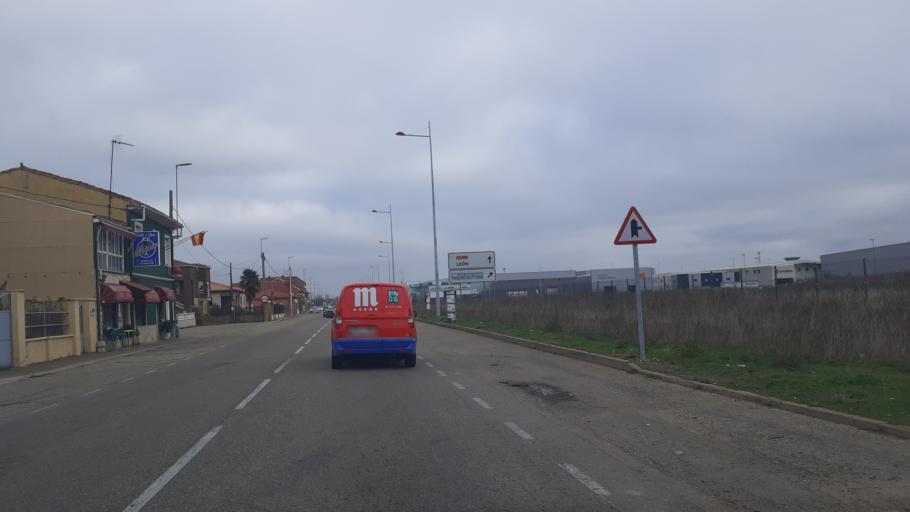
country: ES
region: Castille and Leon
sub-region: Provincia de Leon
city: Onzonilla
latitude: 42.5377
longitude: -5.5908
